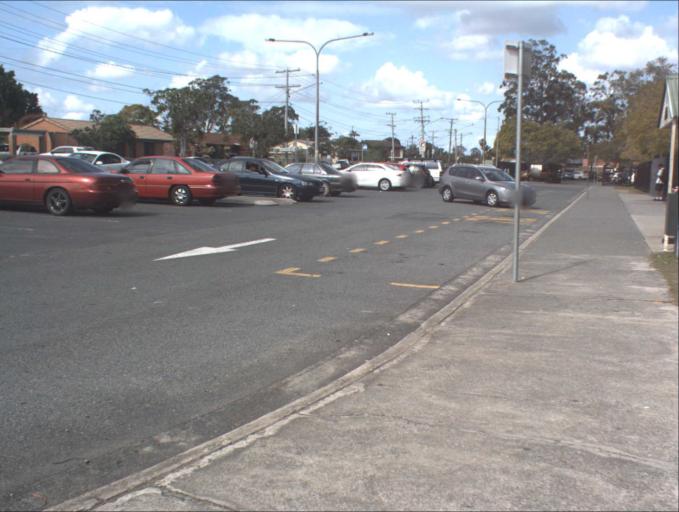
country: AU
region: Queensland
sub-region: Logan
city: Waterford West
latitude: -27.6845
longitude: 153.1110
